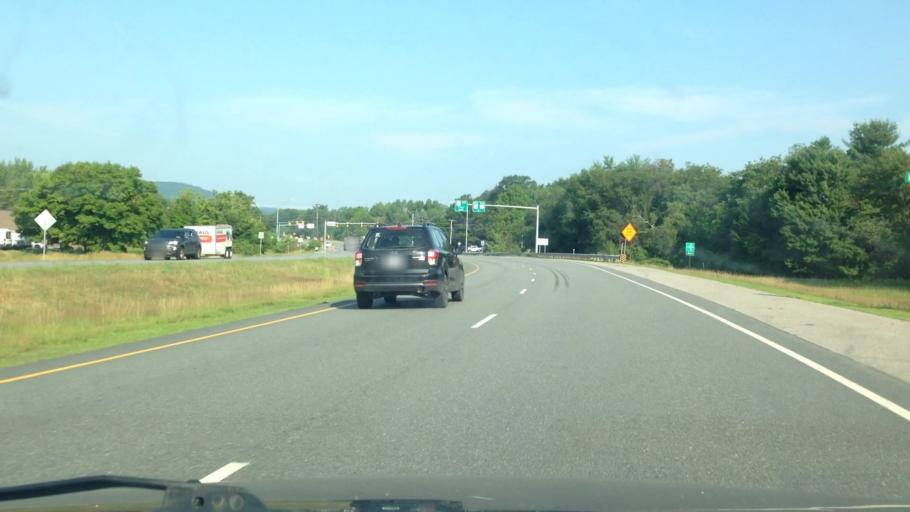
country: US
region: New Hampshire
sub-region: Cheshire County
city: Keene
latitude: 42.9209
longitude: -72.2728
